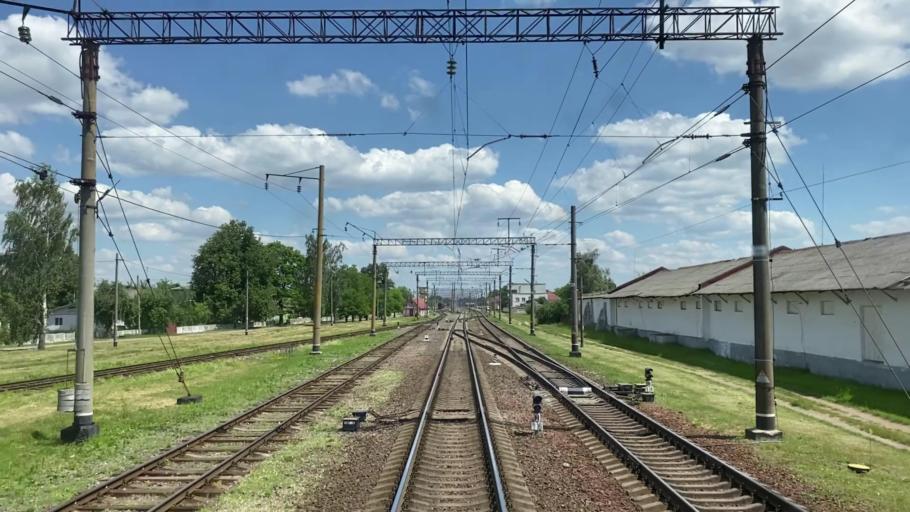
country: BY
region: Brest
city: Byaroza
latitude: 52.5315
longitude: 24.8918
